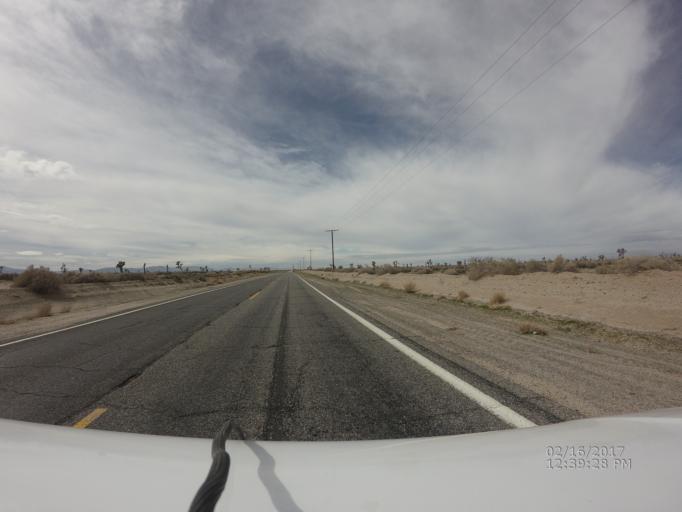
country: US
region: California
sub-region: Los Angeles County
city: Lake Los Angeles
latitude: 34.6753
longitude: -117.8936
